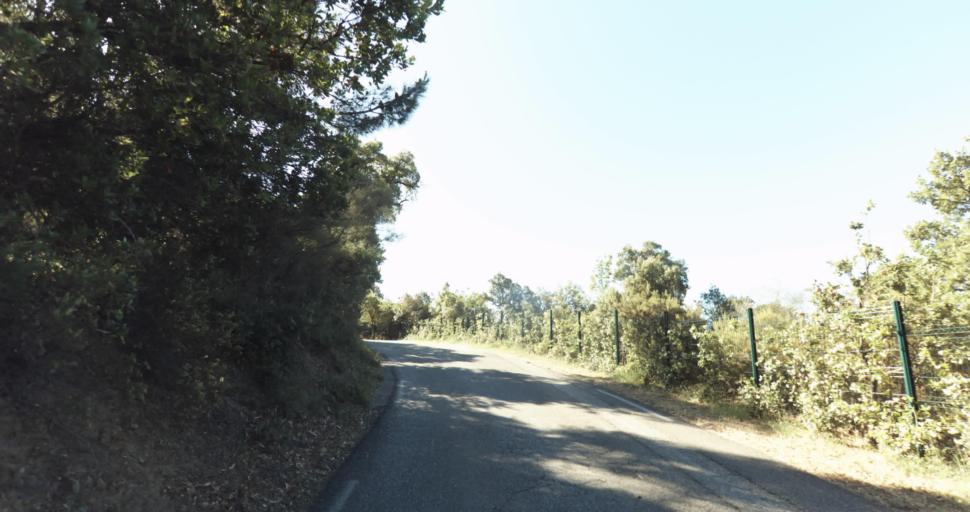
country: FR
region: Provence-Alpes-Cote d'Azur
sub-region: Departement du Var
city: Gassin
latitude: 43.2187
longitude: 6.5958
